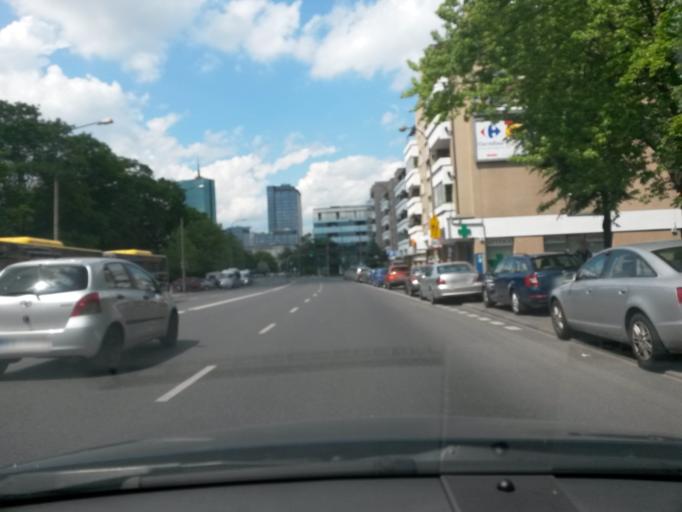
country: PL
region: Masovian Voivodeship
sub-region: Warszawa
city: Wola
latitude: 52.2508
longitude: 21.0034
